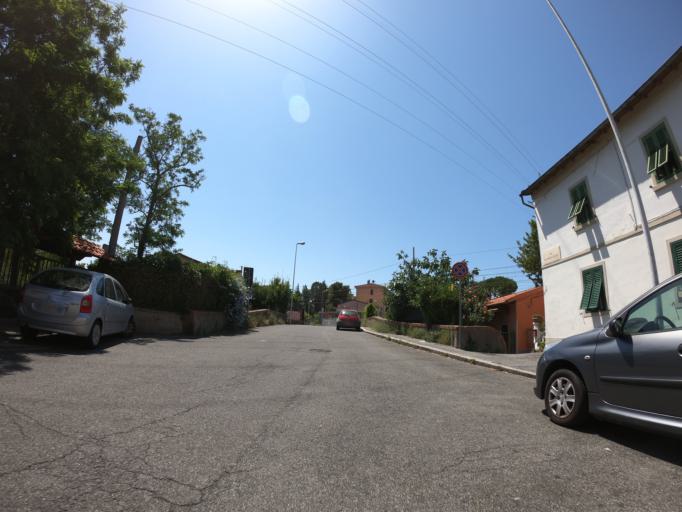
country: IT
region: Tuscany
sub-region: Provincia di Livorno
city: Livorno
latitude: 43.5680
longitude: 10.3325
